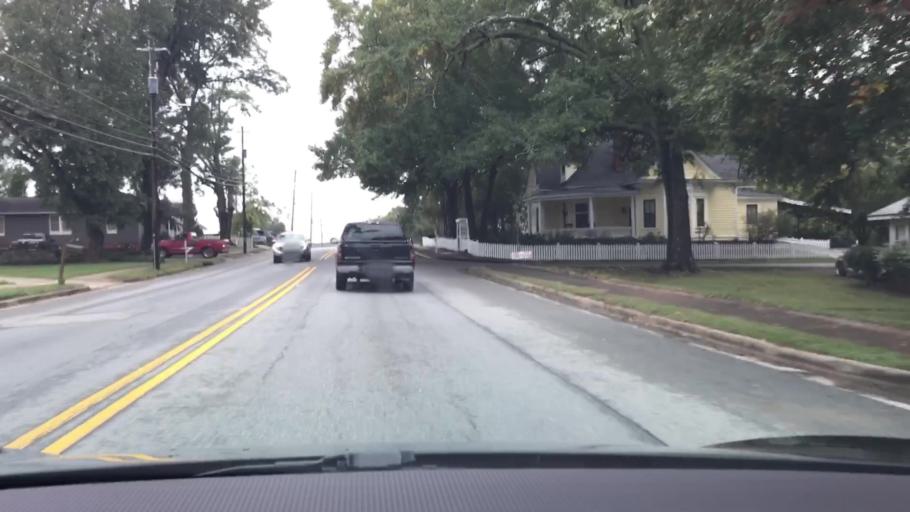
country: US
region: Georgia
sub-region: Greene County
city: Greensboro
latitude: 33.5700
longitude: -83.1833
